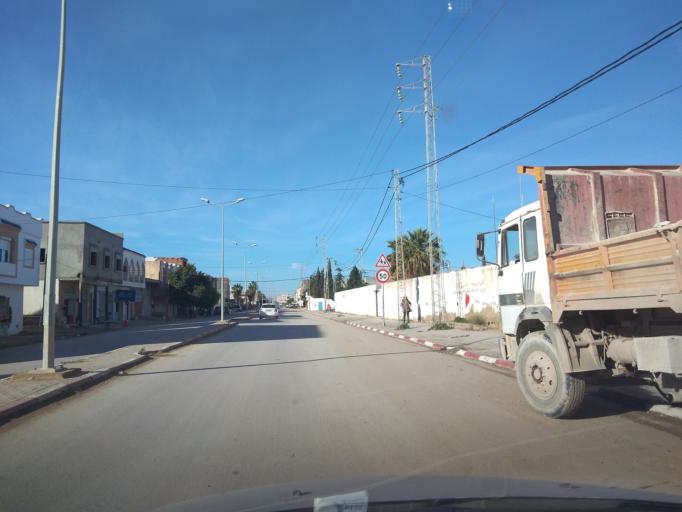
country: TN
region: Ariana
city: Qal'at al Andalus
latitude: 37.0567
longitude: 10.1205
